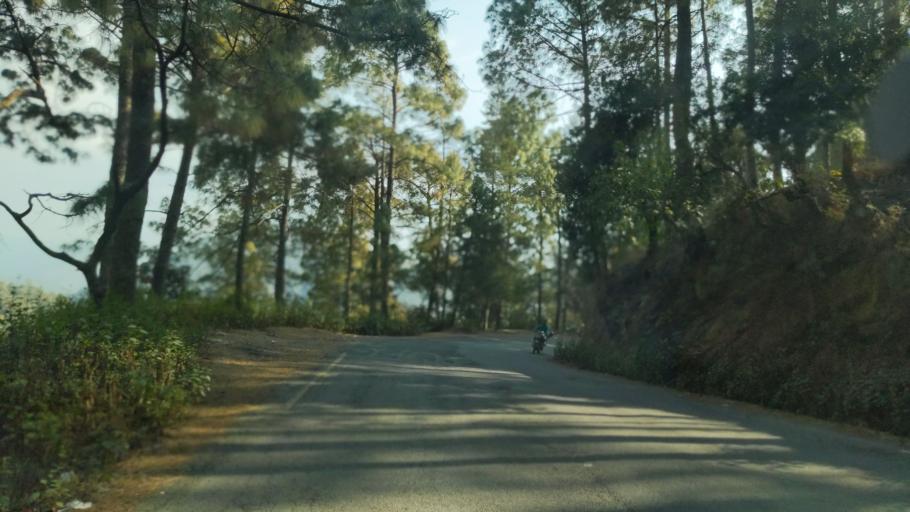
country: IN
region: Uttarakhand
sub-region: Naini Tal
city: Bhowali
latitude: 29.3905
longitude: 79.5397
